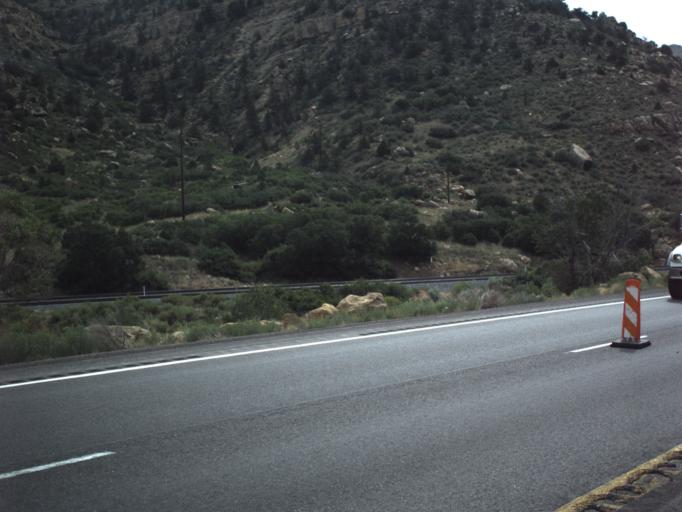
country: US
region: Utah
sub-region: Carbon County
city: Helper
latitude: 39.7827
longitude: -110.9220
